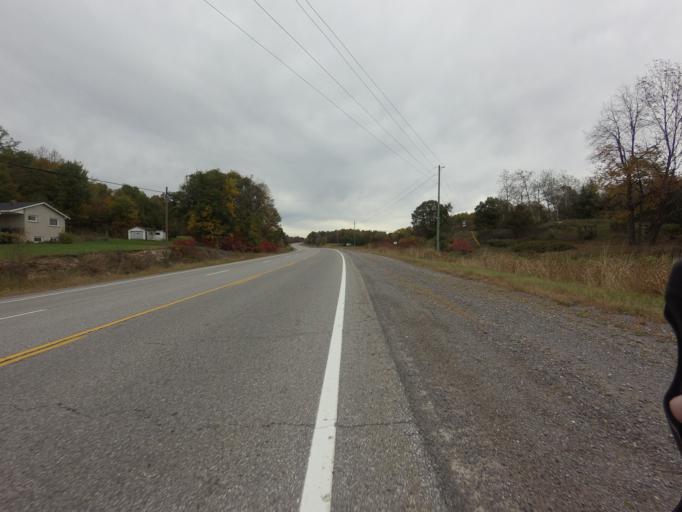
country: CA
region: Ontario
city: Gananoque
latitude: 44.4356
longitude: -76.2846
